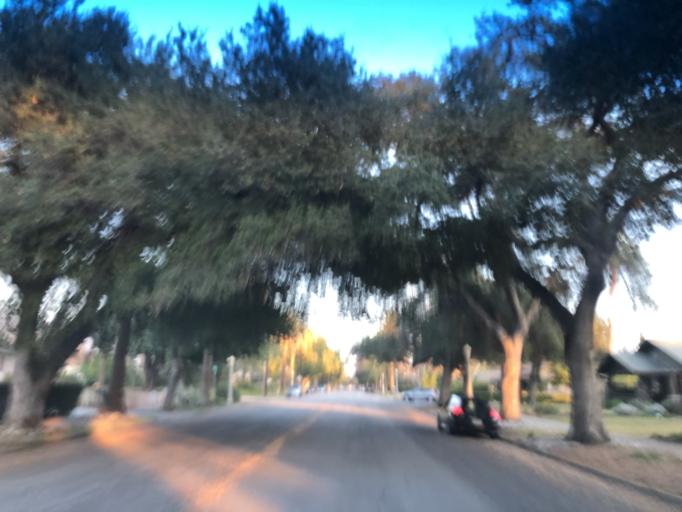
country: US
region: California
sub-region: Los Angeles County
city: East Pasadena
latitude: 34.1565
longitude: -118.1185
